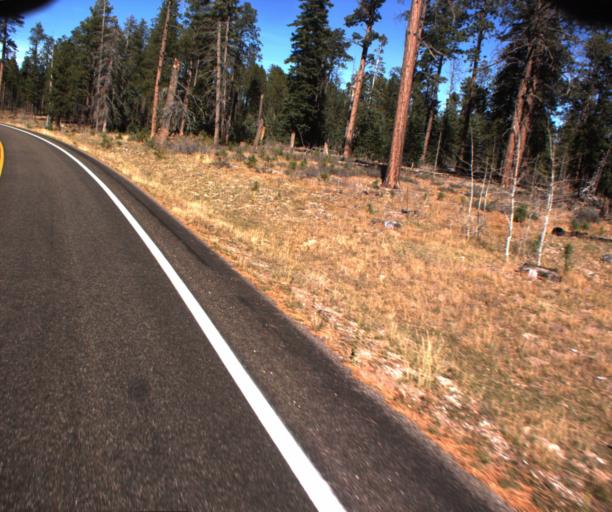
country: US
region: Arizona
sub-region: Coconino County
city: Fredonia
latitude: 36.6367
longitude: -112.1709
